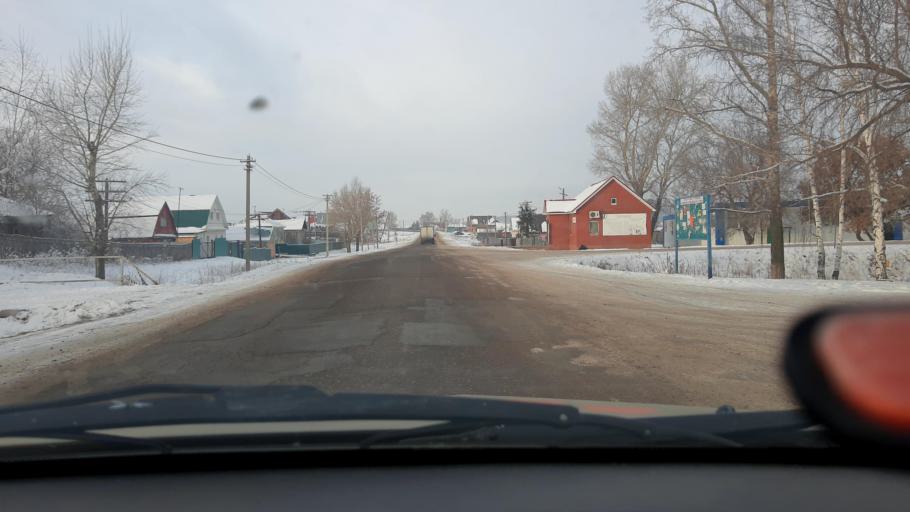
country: RU
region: Bashkortostan
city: Tolbazy
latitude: 54.3570
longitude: 55.8452
